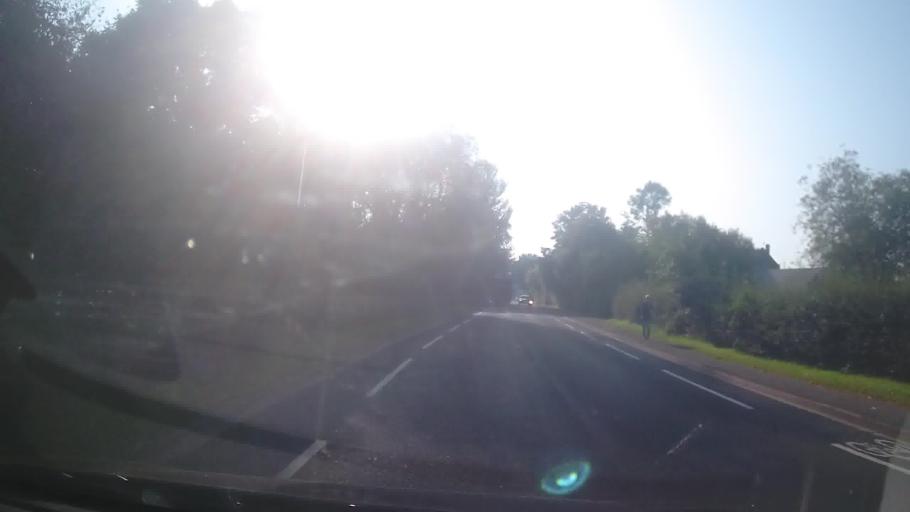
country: GB
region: England
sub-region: Shropshire
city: Astley
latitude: 52.7339
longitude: -2.7163
